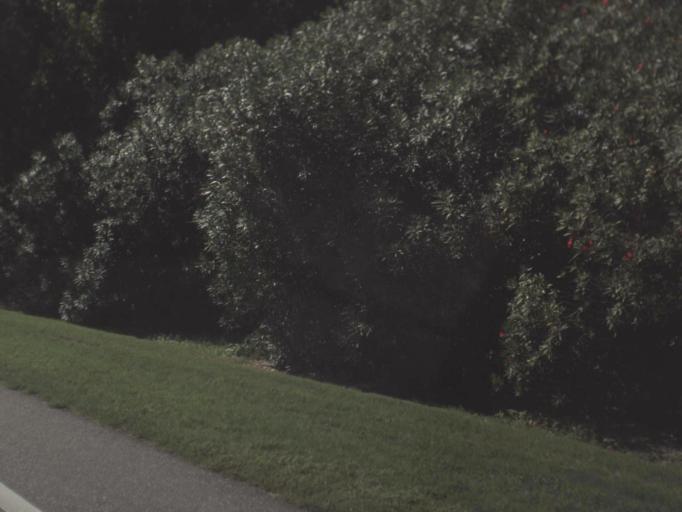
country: US
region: Florida
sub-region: Sarasota County
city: Siesta Key
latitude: 27.3429
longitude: -82.5998
